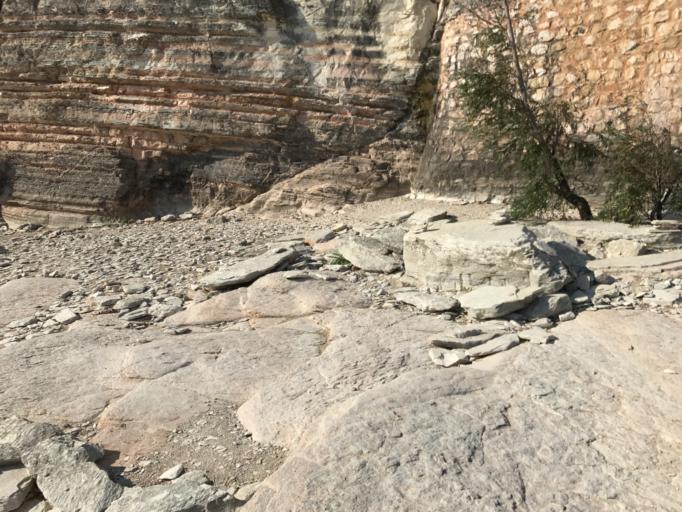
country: IT
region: Lombardy
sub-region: Provincia di Brescia
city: Sirmione
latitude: 45.5013
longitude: 10.6079
